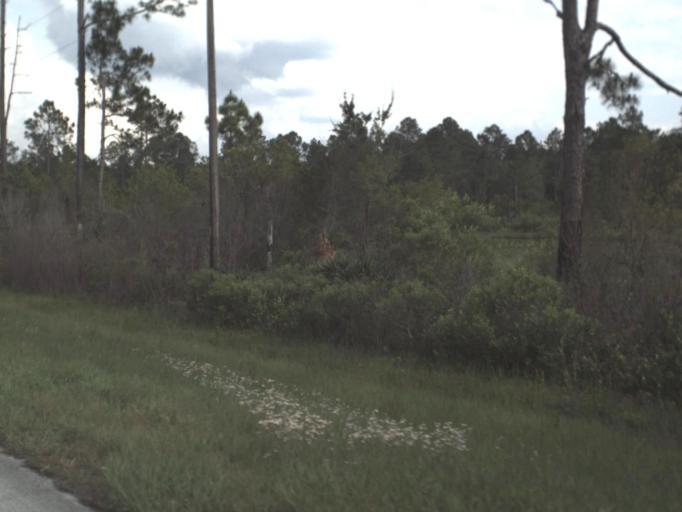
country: US
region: Florida
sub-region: Baker County
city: Macclenny
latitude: 30.5246
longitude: -82.2968
